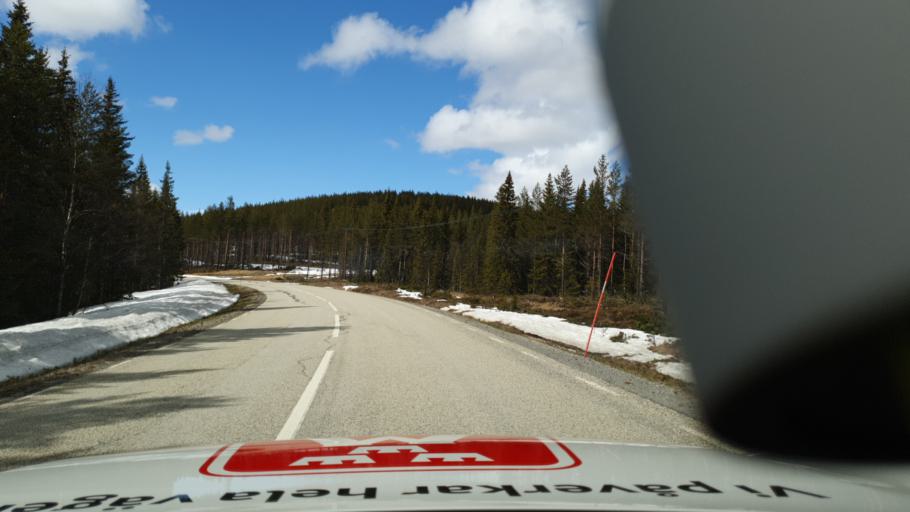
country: SE
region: Jaemtland
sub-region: Are Kommun
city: Are
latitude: 62.8091
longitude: 12.9893
